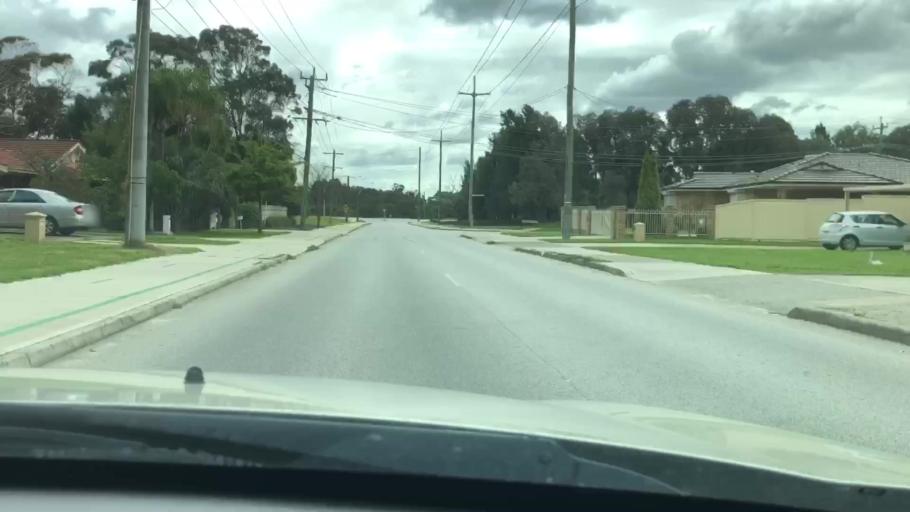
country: AU
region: Western Australia
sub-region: Armadale
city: Seville Grove
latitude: -32.1428
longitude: 115.9779
